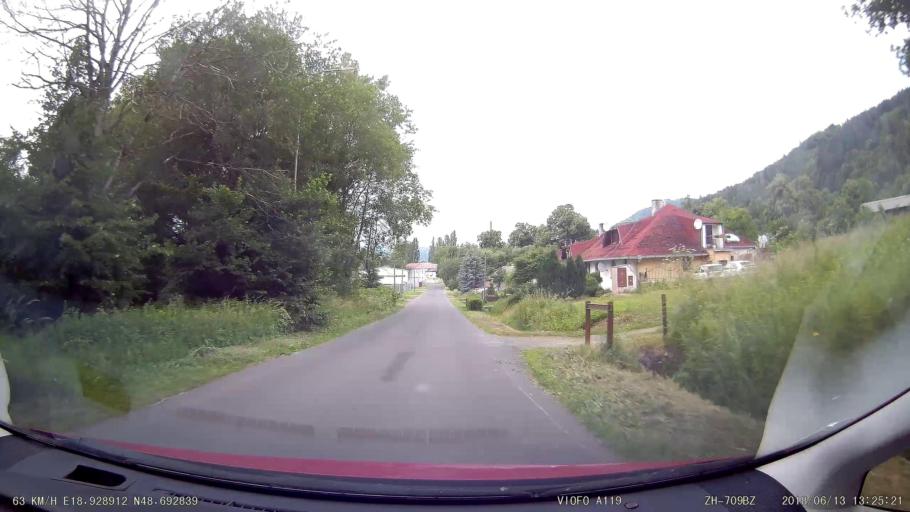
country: SK
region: Banskobystricky
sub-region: Okres Ziar nad Hronom
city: Kremnica
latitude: 48.6929
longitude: 18.9289
